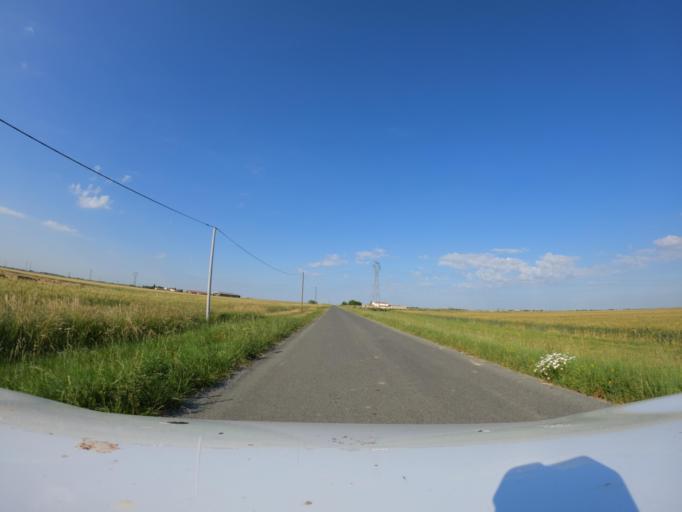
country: FR
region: Poitou-Charentes
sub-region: Departement de la Charente-Maritime
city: Charron
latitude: 46.3342
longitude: -1.0979
